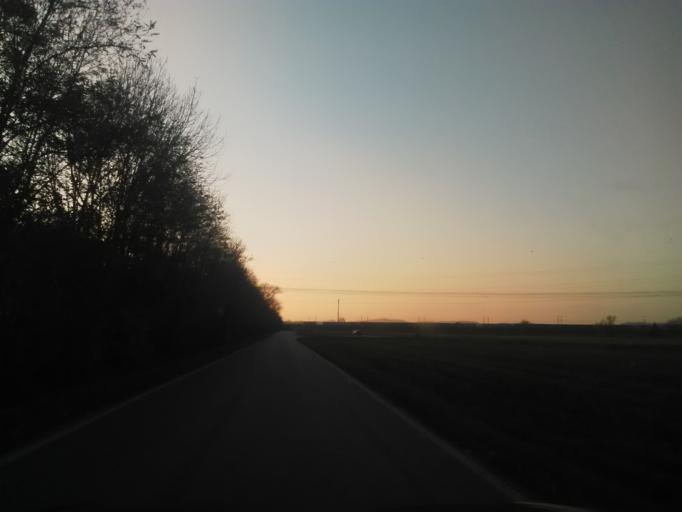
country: IT
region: Piedmont
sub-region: Provincia di Vercelli
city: Santhia
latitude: 45.3609
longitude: 8.1252
